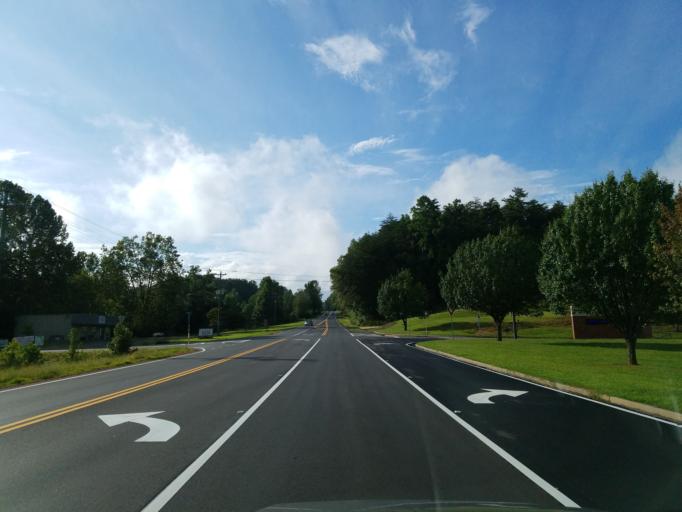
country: US
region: Georgia
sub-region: White County
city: Cleveland
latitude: 34.6166
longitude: -83.7963
